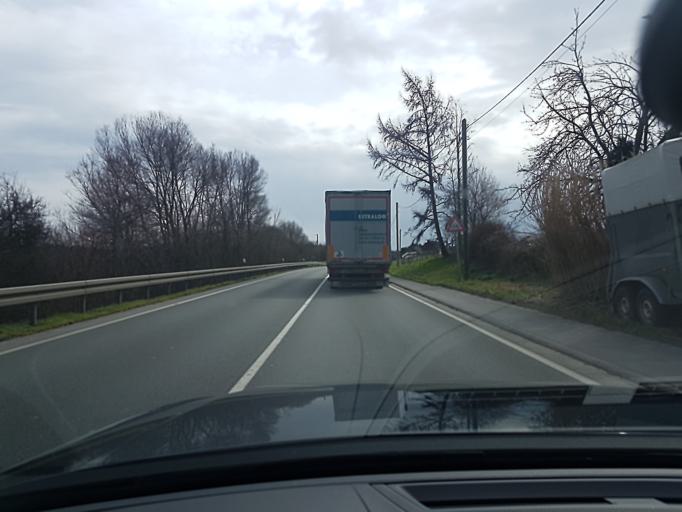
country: DE
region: North Rhine-Westphalia
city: Iserlohn
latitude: 51.4350
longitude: 7.6780
